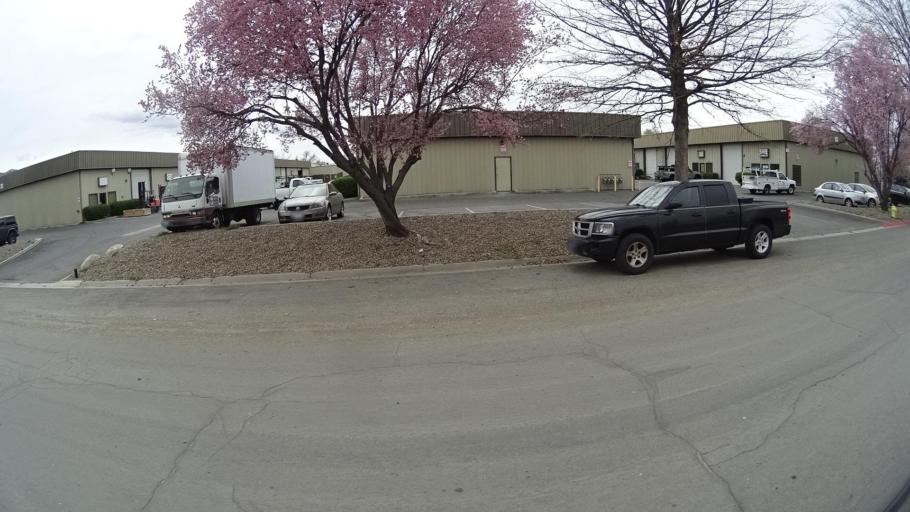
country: US
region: Nevada
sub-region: Washoe County
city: Sparks
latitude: 39.5188
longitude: -119.7381
